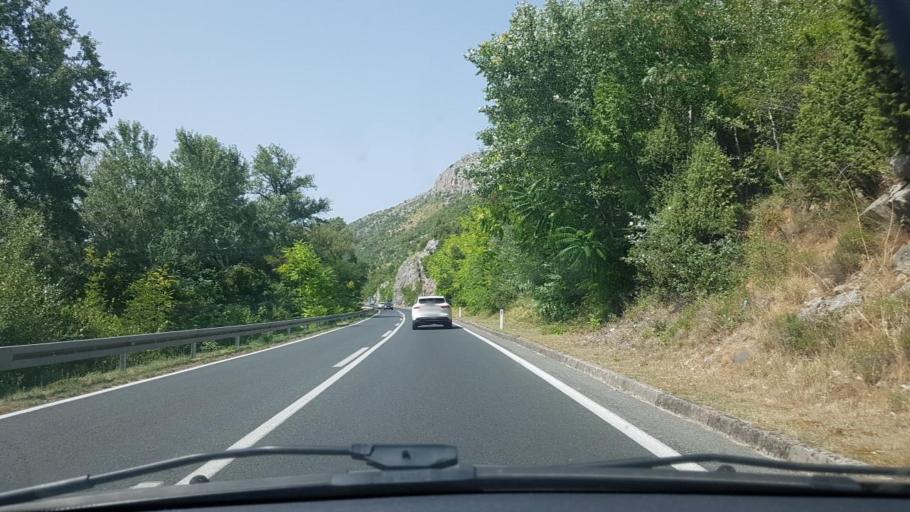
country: BA
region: Federation of Bosnia and Herzegovina
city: Crnici
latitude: 43.1771
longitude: 17.7868
